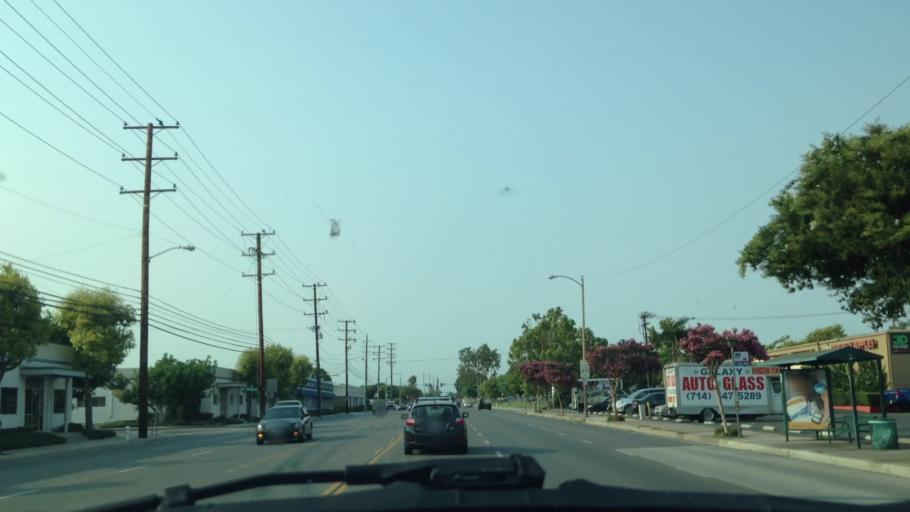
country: US
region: California
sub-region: Orange County
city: Santa Ana
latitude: 33.7274
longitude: -117.8505
